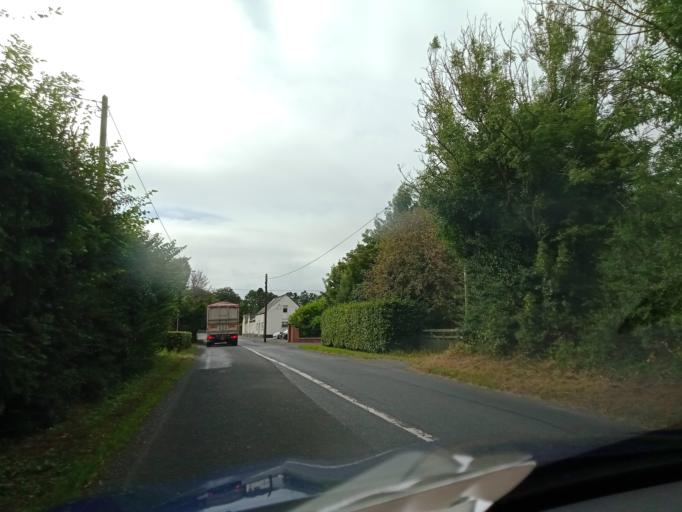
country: IE
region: Leinster
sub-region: Laois
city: Portlaoise
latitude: 53.0166
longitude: -7.2985
